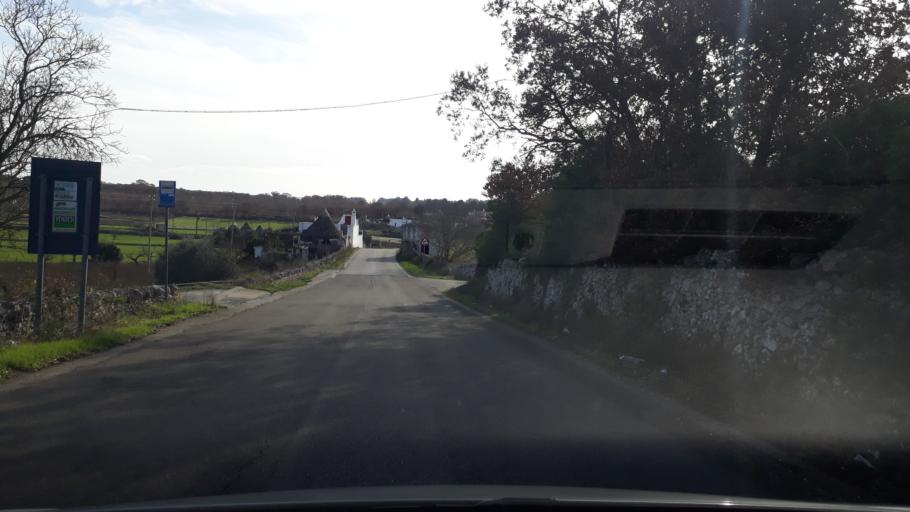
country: IT
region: Apulia
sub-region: Provincia di Taranto
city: Martina Franca
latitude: 40.6814
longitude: 17.3545
